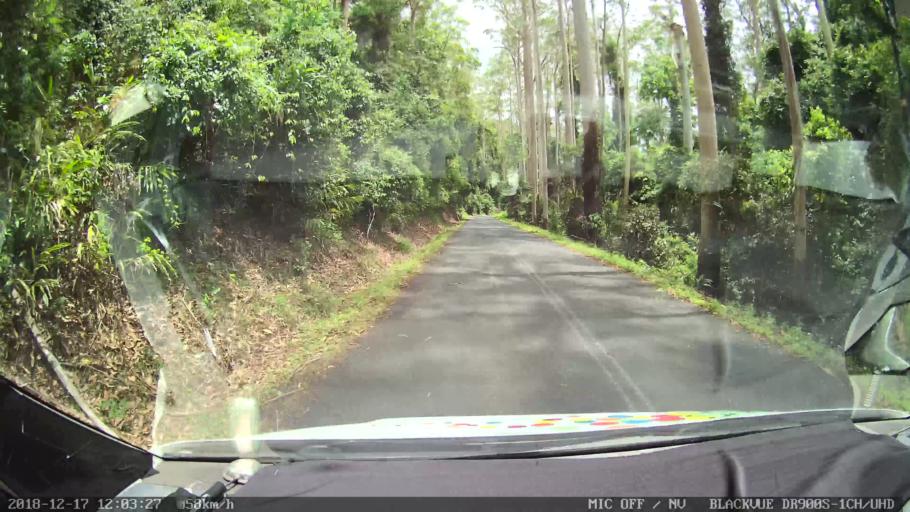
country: AU
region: New South Wales
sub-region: Kyogle
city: Kyogle
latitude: -28.5081
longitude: 152.5681
